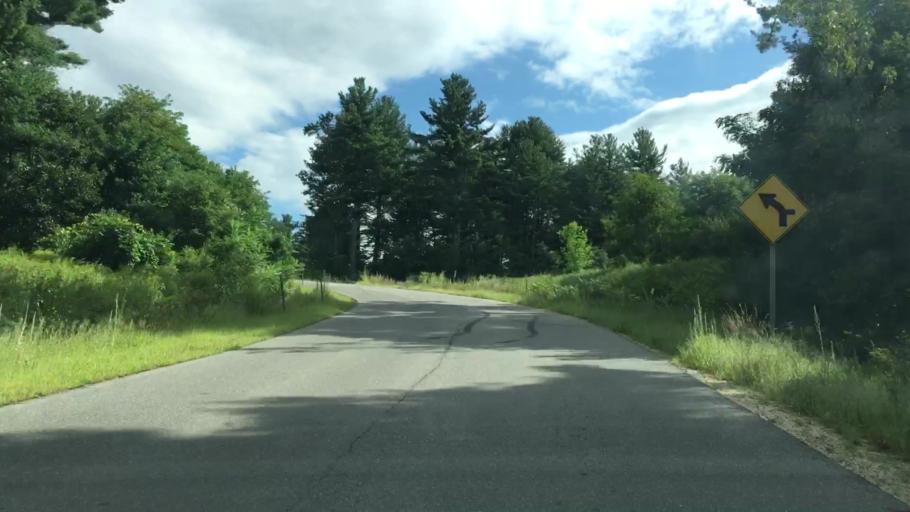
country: US
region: New Hampshire
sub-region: Strafford County
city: Madbury
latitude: 43.1703
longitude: -70.9198
